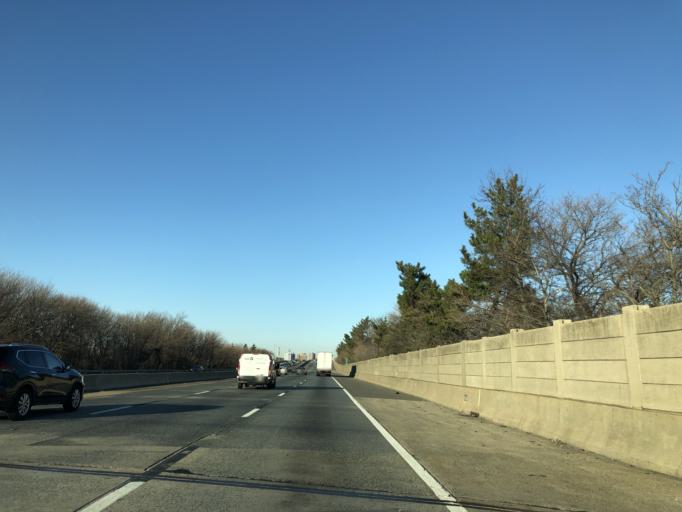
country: US
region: New Jersey
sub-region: Camden County
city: Camden
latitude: 39.9212
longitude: -75.1161
